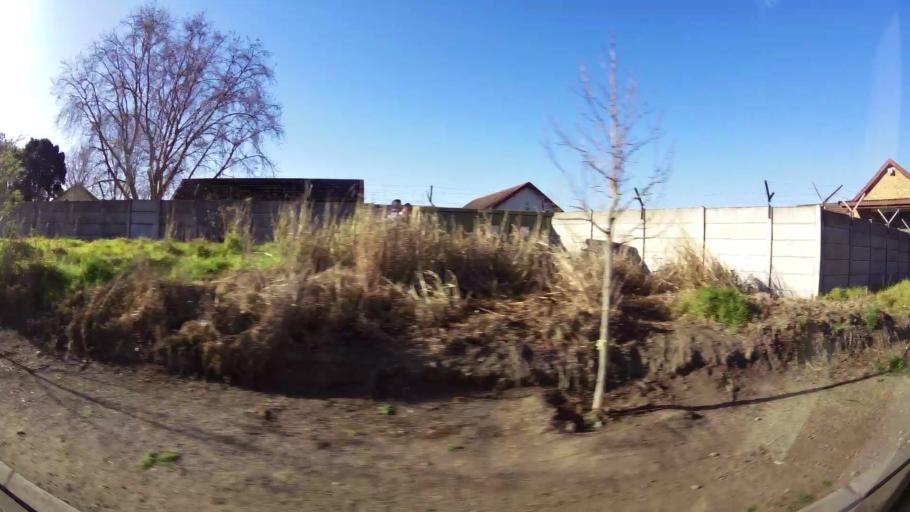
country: ZA
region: Western Cape
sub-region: Eden District Municipality
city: George
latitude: -33.9571
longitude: 22.4453
